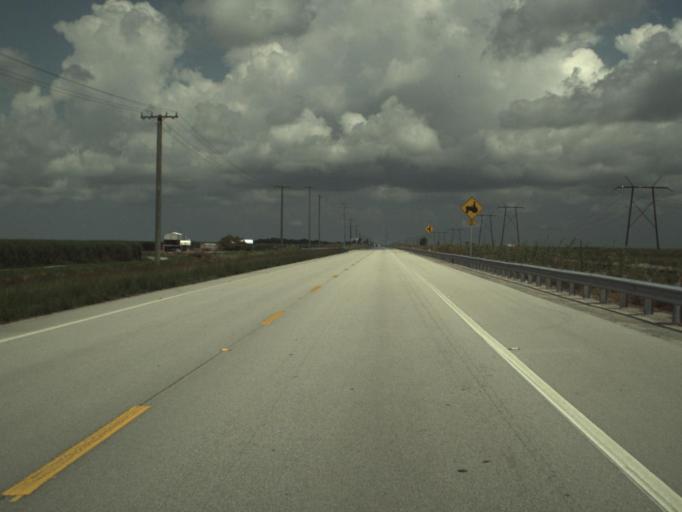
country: US
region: Florida
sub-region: Palm Beach County
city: Pahokee
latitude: 26.7494
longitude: -80.4794
